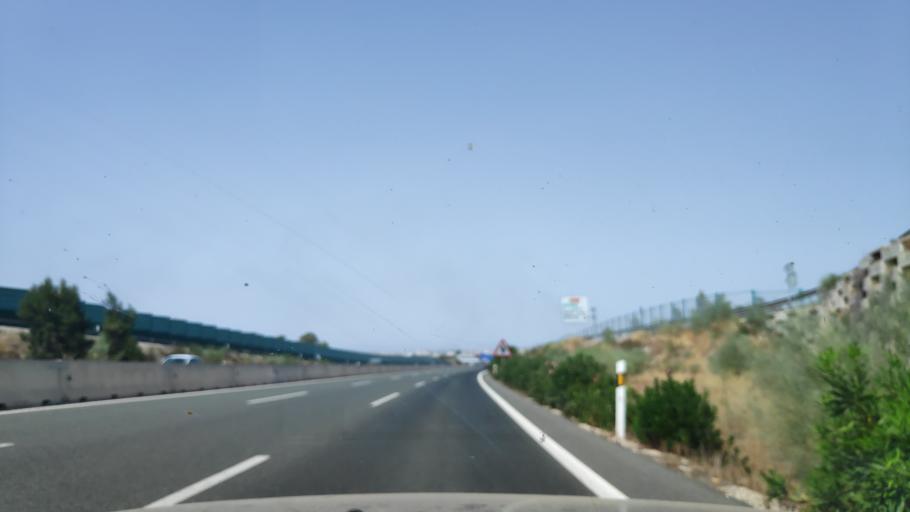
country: ES
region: Murcia
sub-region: Murcia
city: Murcia
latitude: 37.9360
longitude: -1.1530
